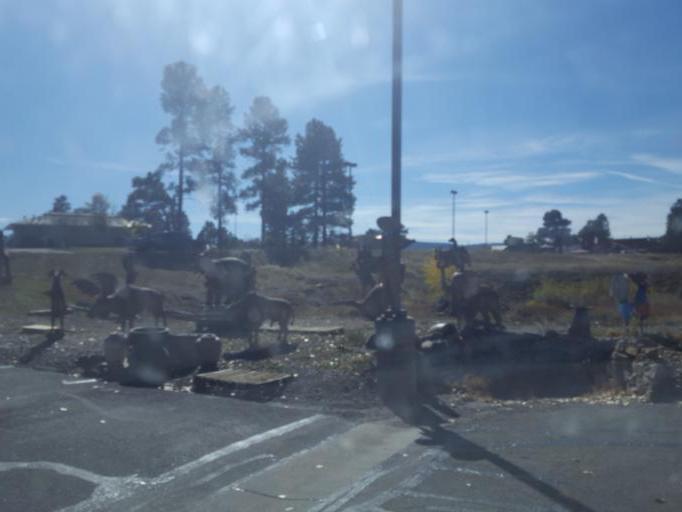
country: US
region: Colorado
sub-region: Archuleta County
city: Pagosa Springs
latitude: 37.2561
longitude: -107.0775
